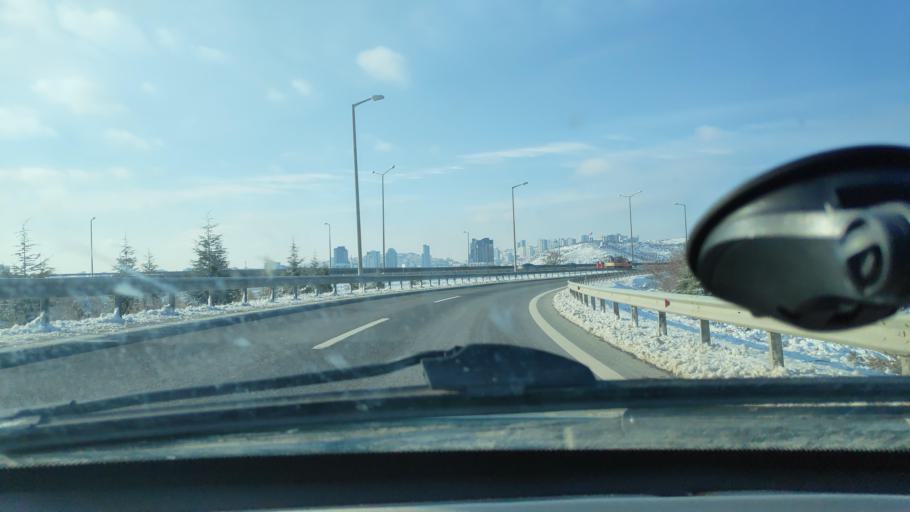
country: TR
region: Ankara
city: Ankara
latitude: 40.0231
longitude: 32.8286
